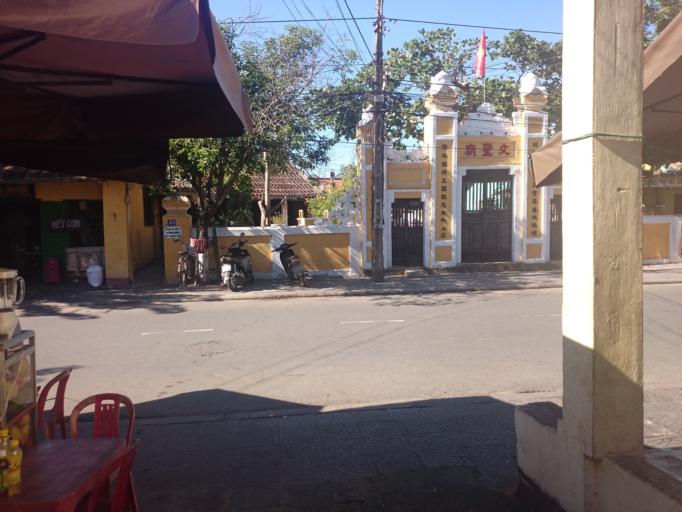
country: VN
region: Quang Nam
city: Hoi An
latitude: 15.8784
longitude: 108.3305
